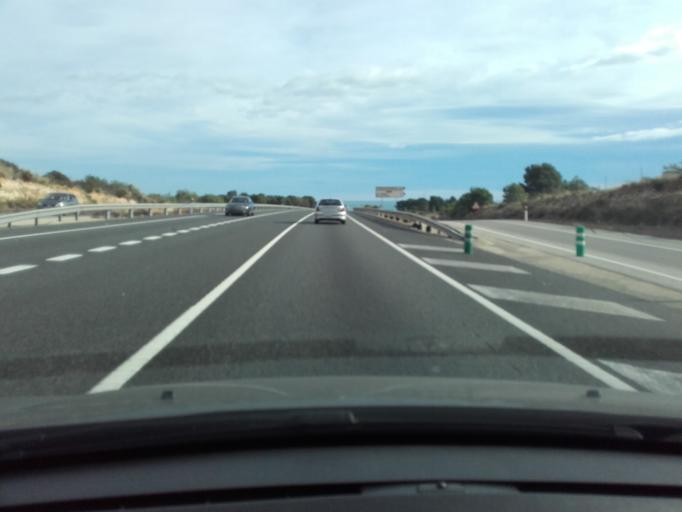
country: ES
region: Catalonia
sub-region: Provincia de Tarragona
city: Torredembarra
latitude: 41.1615
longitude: 1.4132
